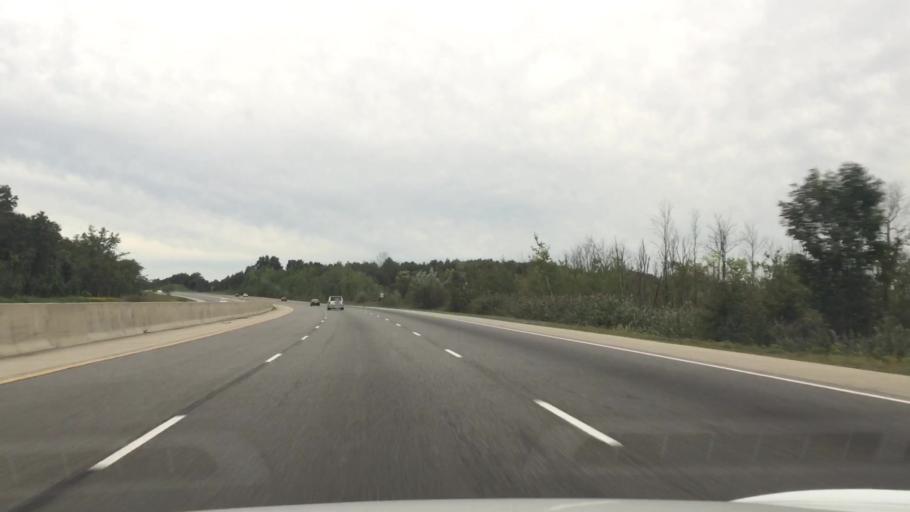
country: CA
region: Ontario
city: Kitchener
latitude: 43.2584
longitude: -80.5651
